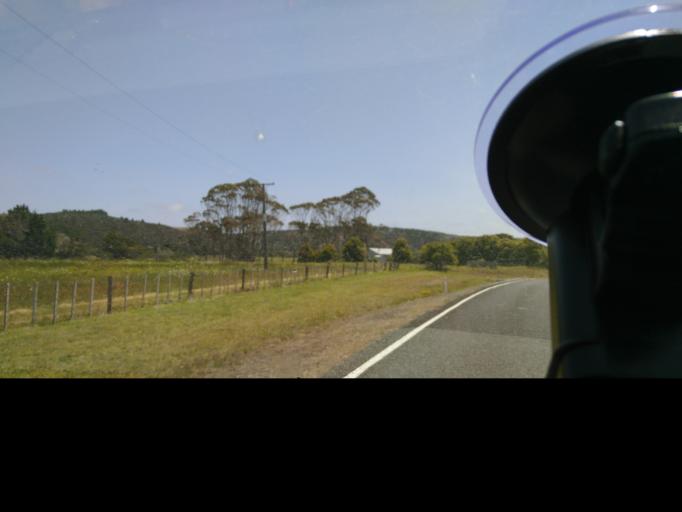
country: NZ
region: Northland
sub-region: Far North District
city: Kaitaia
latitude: -34.6264
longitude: 172.9646
